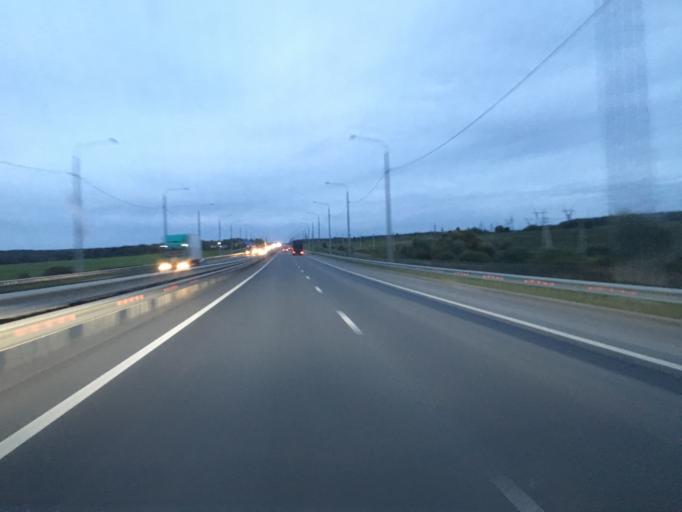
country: RU
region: Kaluga
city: Maloyaroslavets
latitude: 54.9488
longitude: 36.4435
